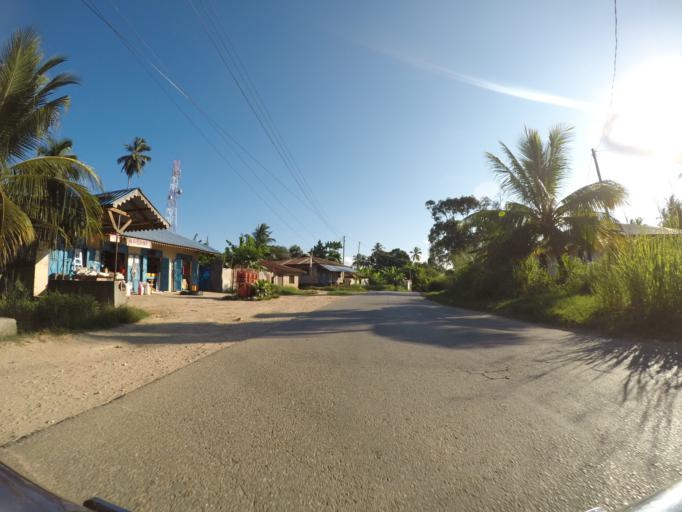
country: TZ
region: Pemba South
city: Chake Chake
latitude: -5.2960
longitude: 39.7595
